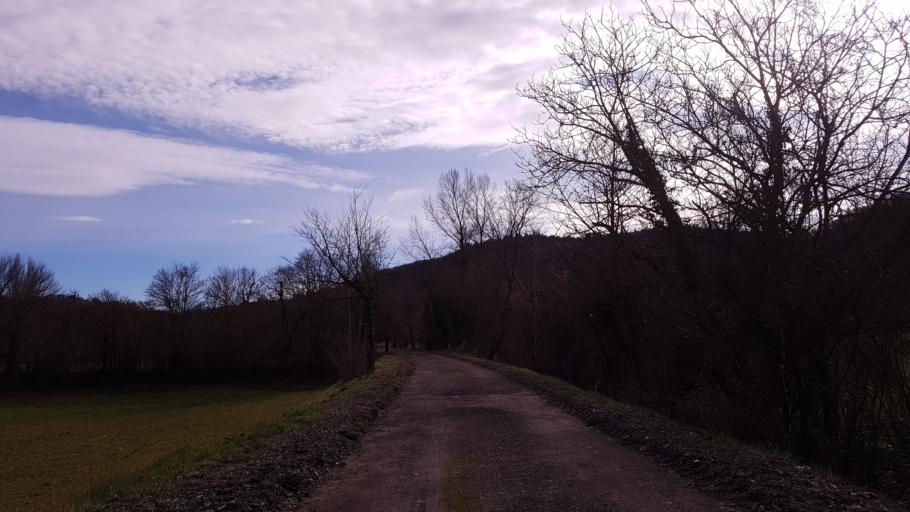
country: FR
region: Languedoc-Roussillon
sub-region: Departement de l'Aude
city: Chalabre
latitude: 43.0049
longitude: 1.9875
